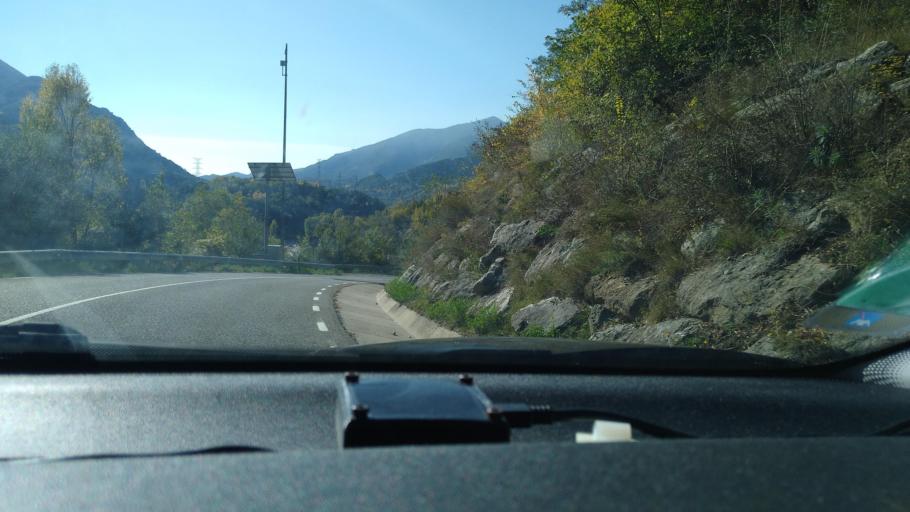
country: ES
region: Catalonia
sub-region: Provincia de Barcelona
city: Vallcebre
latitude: 42.1801
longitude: 1.8612
